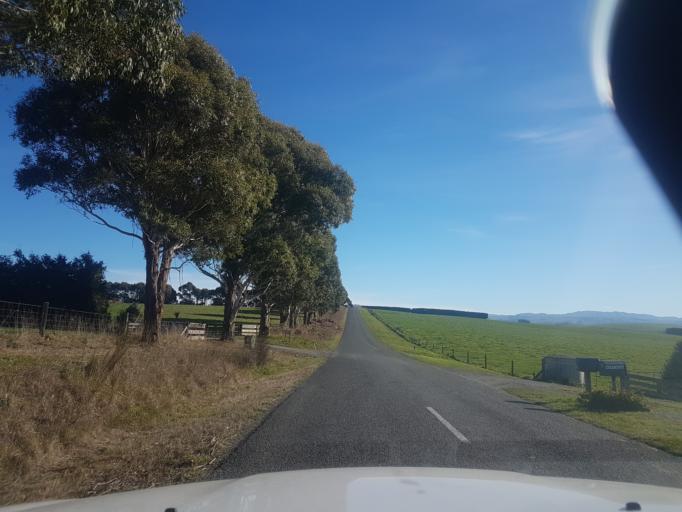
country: NZ
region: Canterbury
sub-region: Timaru District
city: Pleasant Point
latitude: -44.2475
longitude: 171.0792
